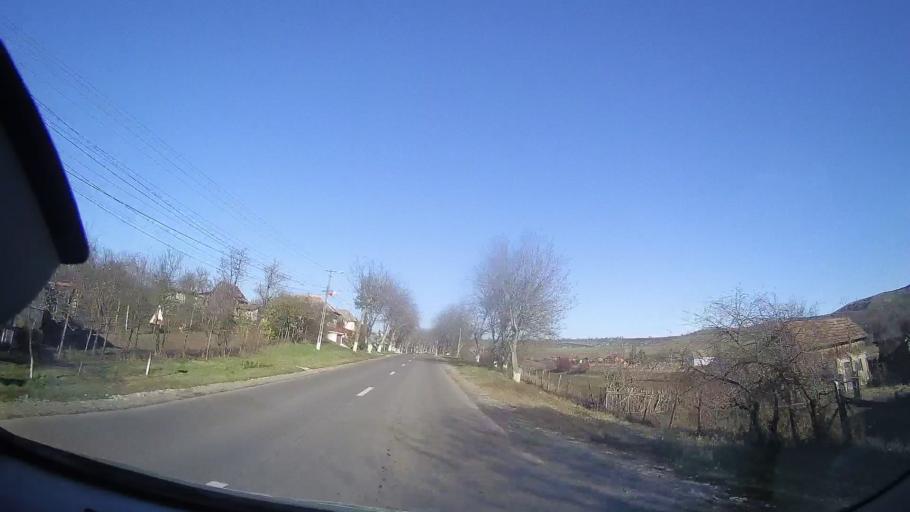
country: RO
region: Mures
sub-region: Comuna Sarmasu
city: Balda
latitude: 46.7331
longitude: 24.1472
